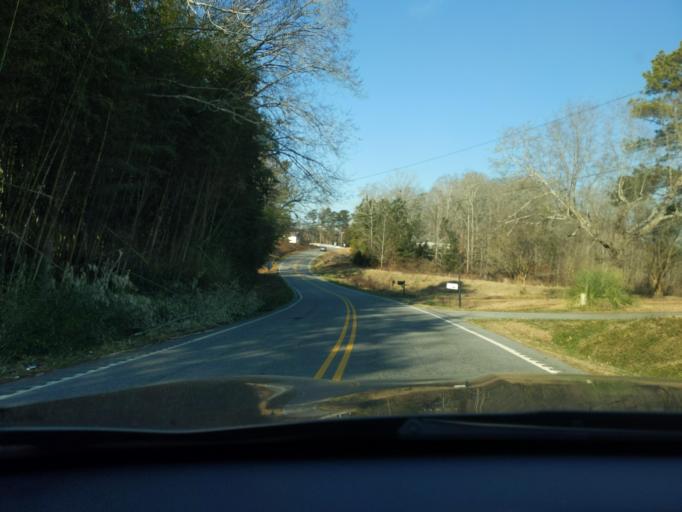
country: US
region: South Carolina
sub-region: Greenwood County
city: Greenwood
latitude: 34.1811
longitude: -82.0992
